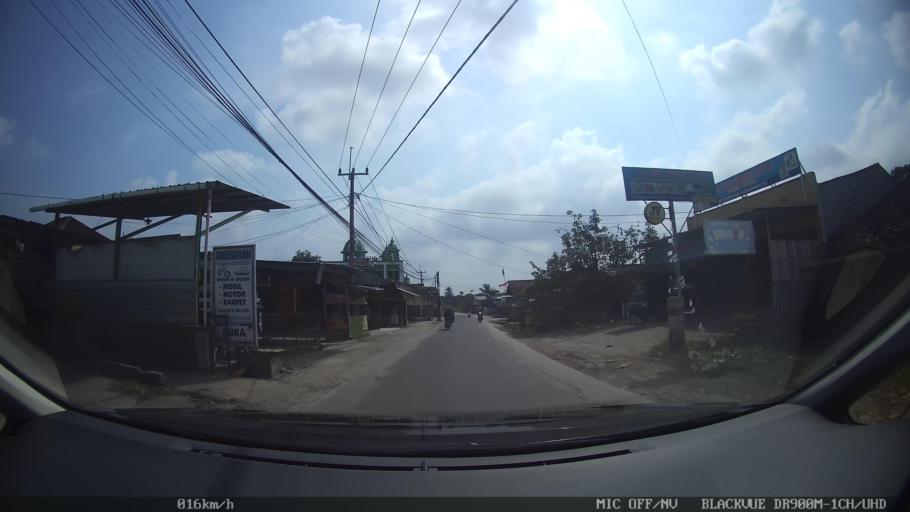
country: ID
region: Lampung
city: Kedaton
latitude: -5.3514
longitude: 105.2635
